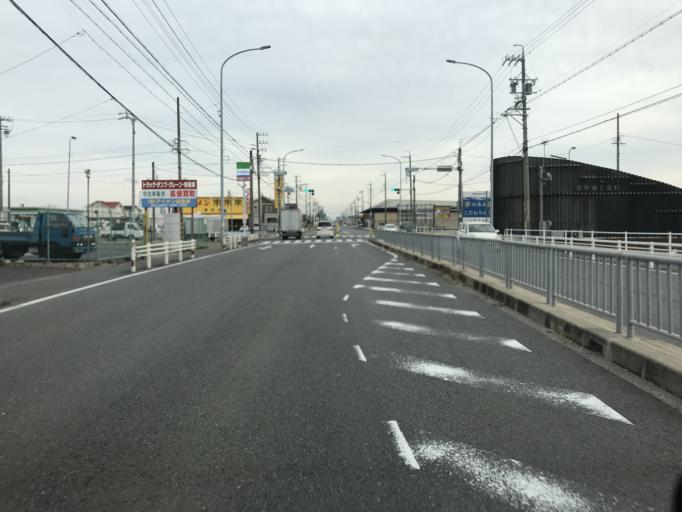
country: JP
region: Aichi
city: Kanie
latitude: 35.1848
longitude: 136.7925
